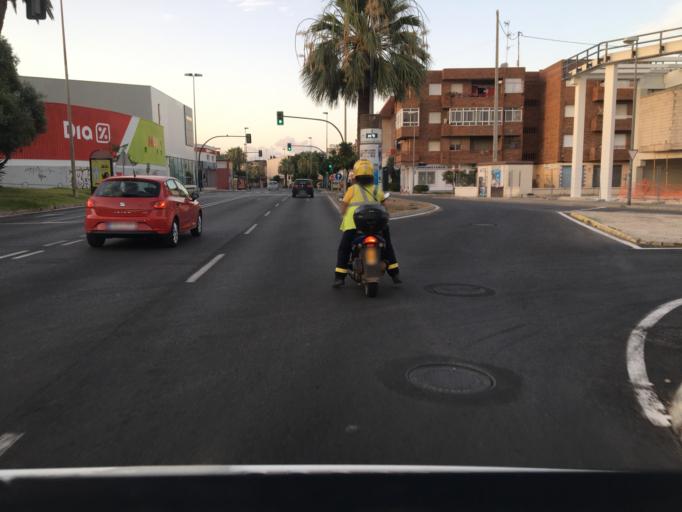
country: ES
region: Murcia
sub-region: Murcia
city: Cartagena
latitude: 37.6274
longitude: -1.0019
